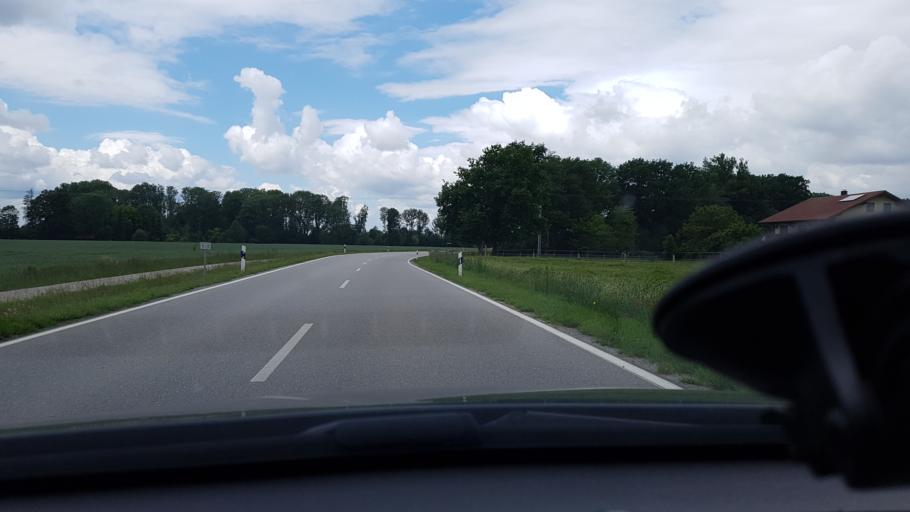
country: DE
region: Bavaria
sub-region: Lower Bavaria
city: Pocking
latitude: 48.4056
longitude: 13.3791
